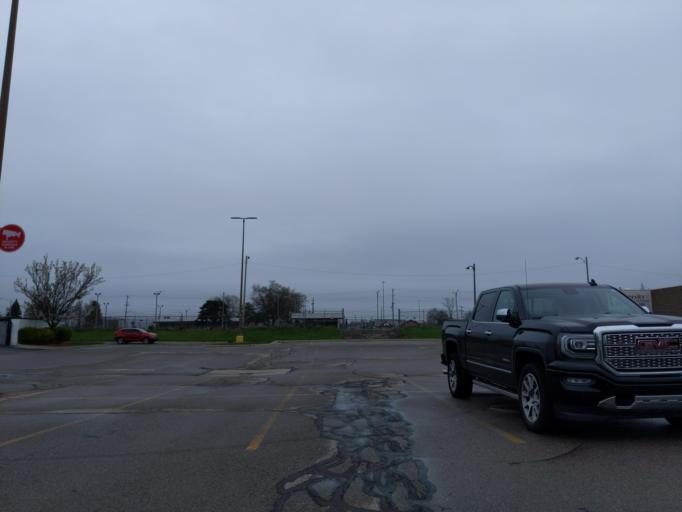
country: US
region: Michigan
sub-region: Ingham County
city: Holt
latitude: 42.6639
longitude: -84.5435
